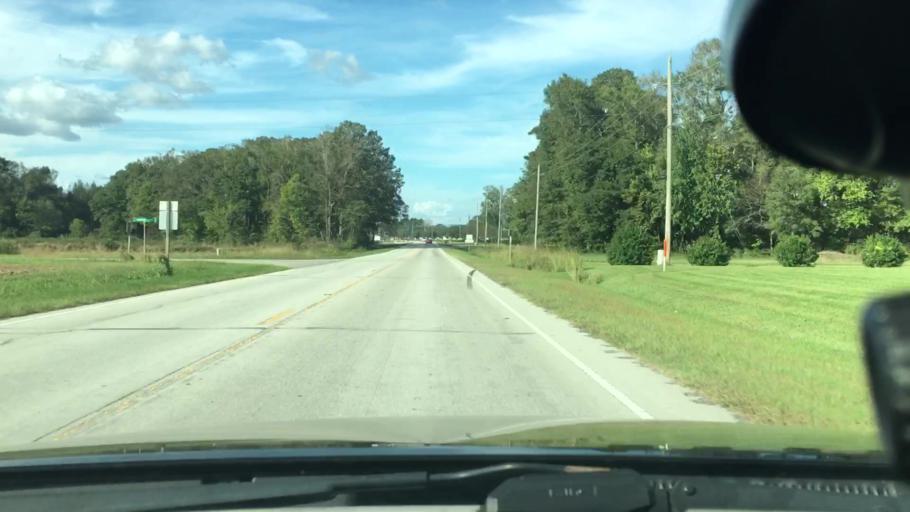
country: US
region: North Carolina
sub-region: Pitt County
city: Windsor
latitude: 35.5229
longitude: -77.3192
